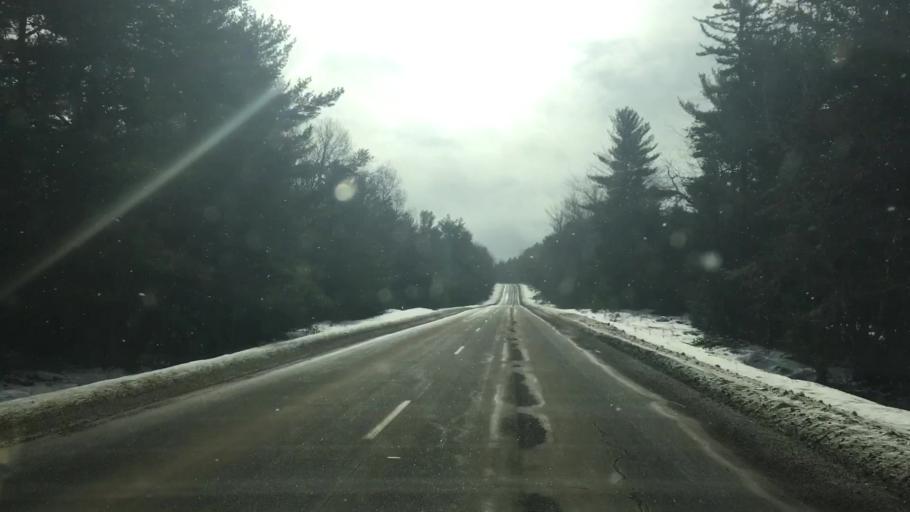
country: US
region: Maine
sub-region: Washington County
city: Calais
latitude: 45.0724
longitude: -67.3318
